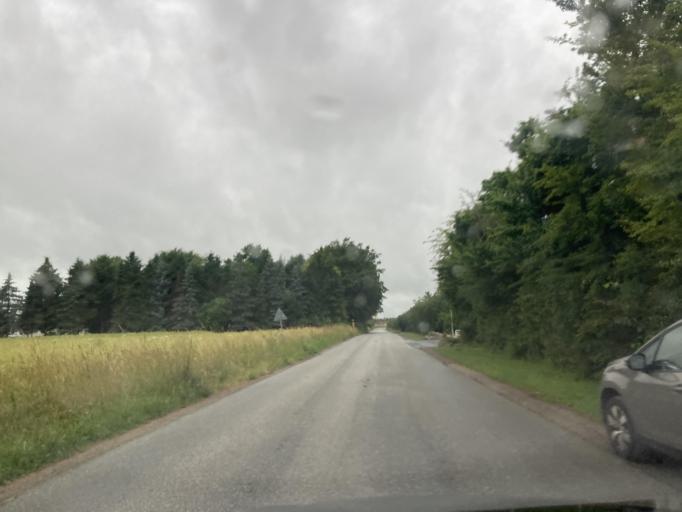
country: DK
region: Zealand
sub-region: Roskilde Kommune
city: Svogerslev
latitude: 55.6113
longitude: 12.0460
